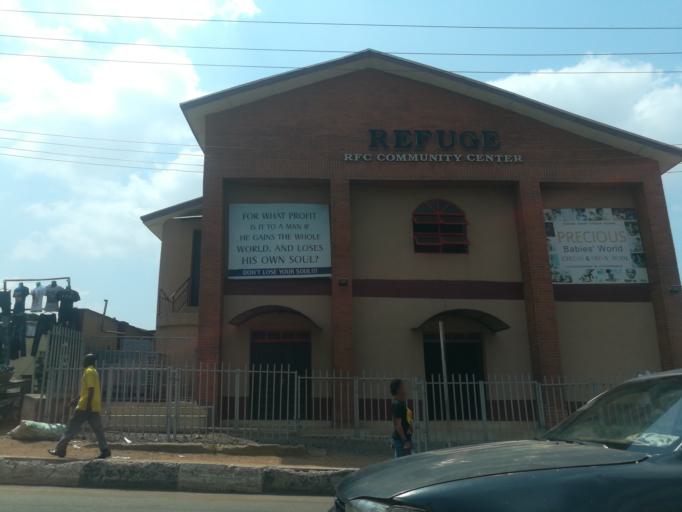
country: NG
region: Ogun
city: Abeokuta
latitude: 7.1478
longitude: 3.3611
